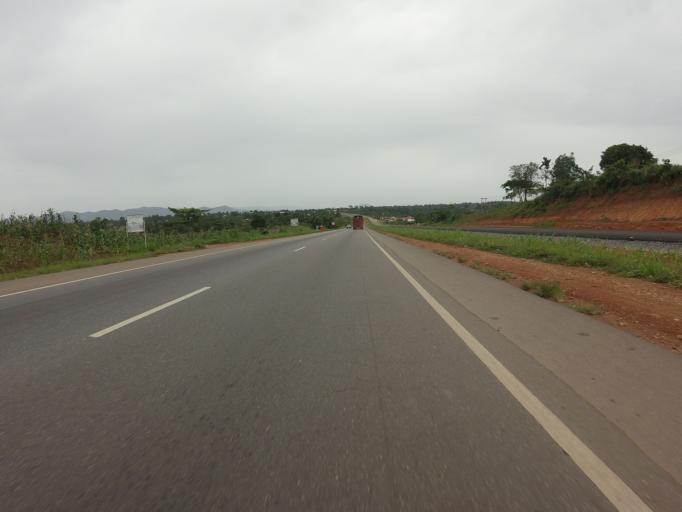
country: GH
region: Eastern
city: Suhum
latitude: 6.0575
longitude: -0.4650
